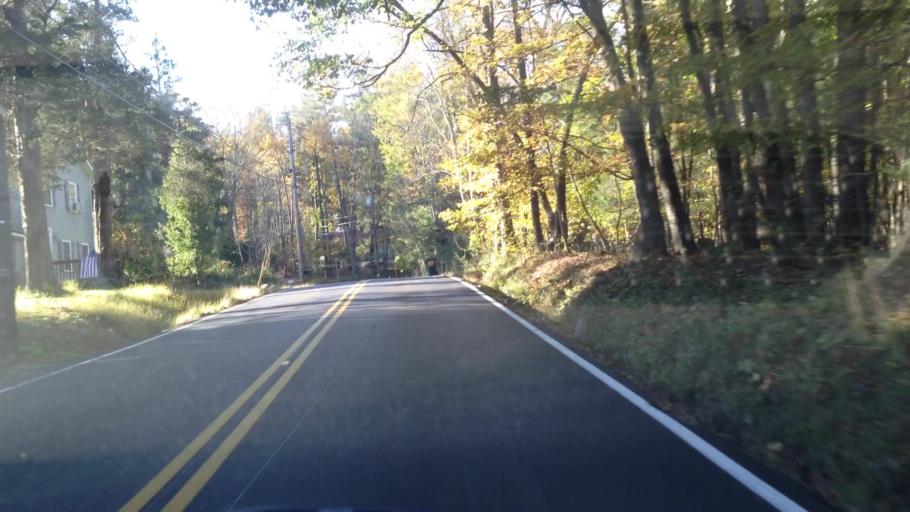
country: US
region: New York
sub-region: Ulster County
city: Tillson
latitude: 41.8309
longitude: -74.0401
